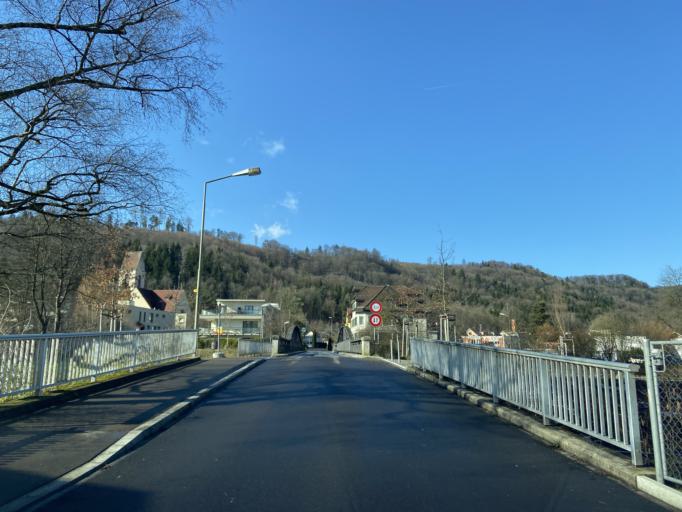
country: CH
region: Zurich
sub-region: Bezirk Winterthur
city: Toess (Kreis 4) / Schlosstal
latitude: 47.4937
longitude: 8.7045
